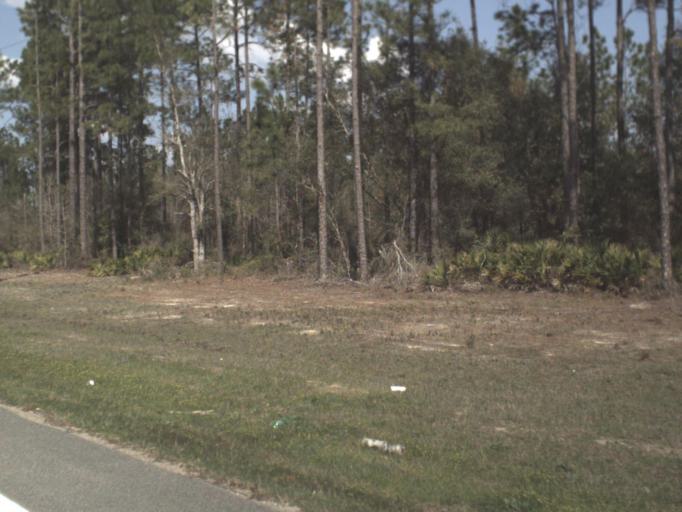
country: US
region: Florida
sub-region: Liberty County
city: Bristol
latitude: 30.4055
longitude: -84.8269
